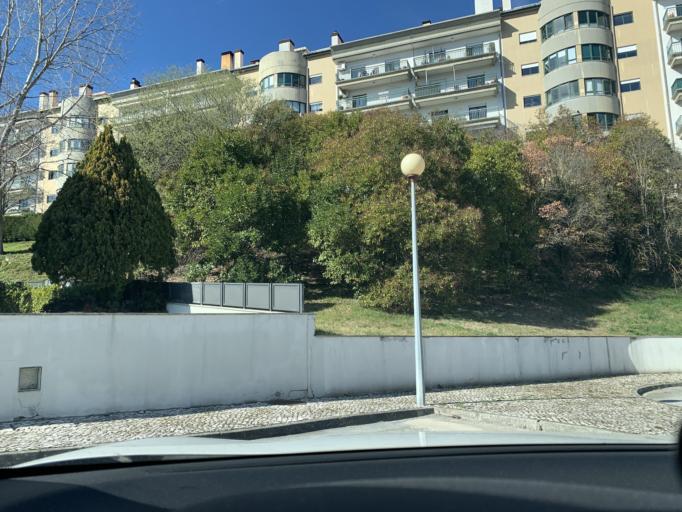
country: PT
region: Viseu
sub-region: Viseu
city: Viseu
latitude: 40.6360
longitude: -7.9272
